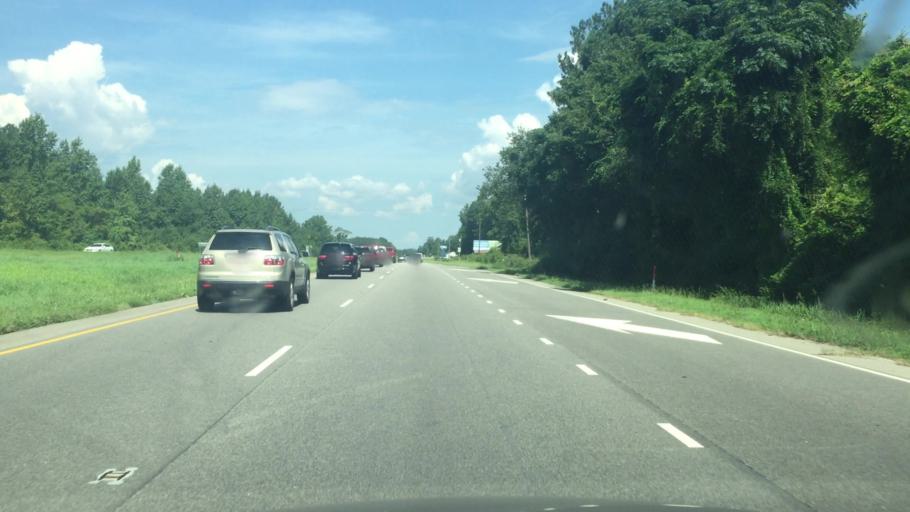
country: US
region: North Carolina
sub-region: Scotland County
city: Laurinburg
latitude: 34.7894
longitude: -79.5061
